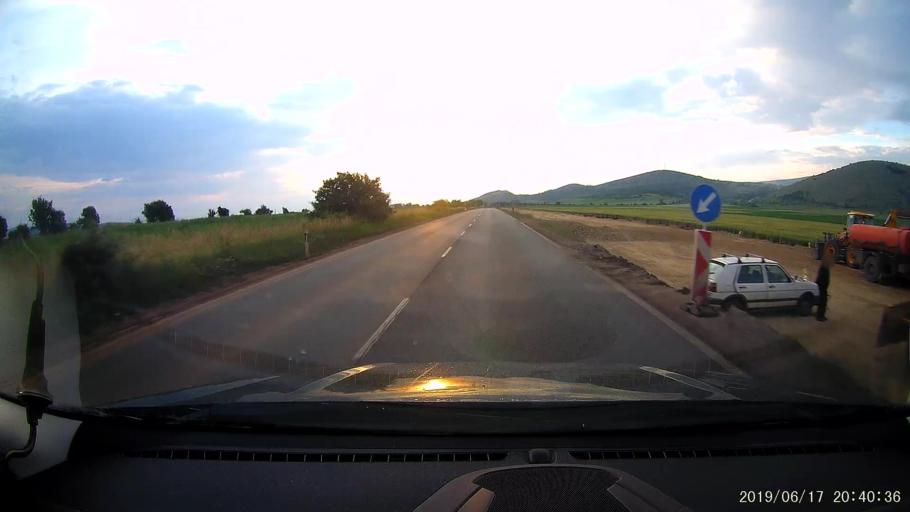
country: BG
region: Sofiya
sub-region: Obshtina Dragoman
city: Dragoman
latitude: 42.8884
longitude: 22.9835
